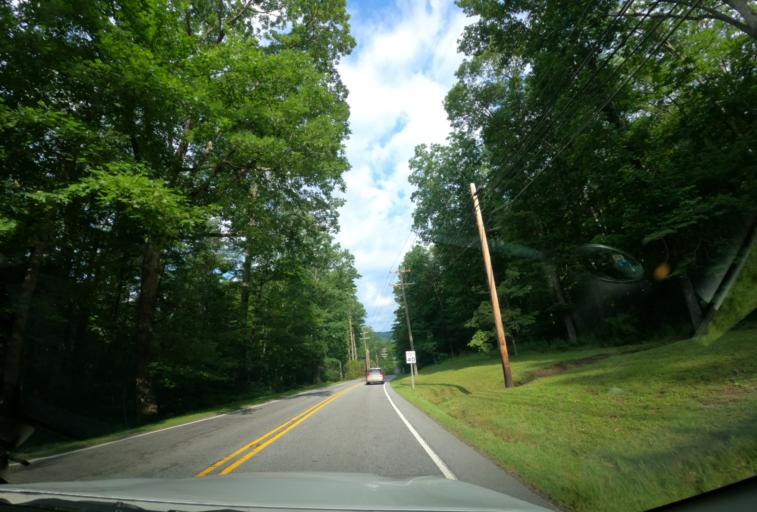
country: US
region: North Carolina
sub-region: Jackson County
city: Cullowhee
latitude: 35.1219
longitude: -83.0485
